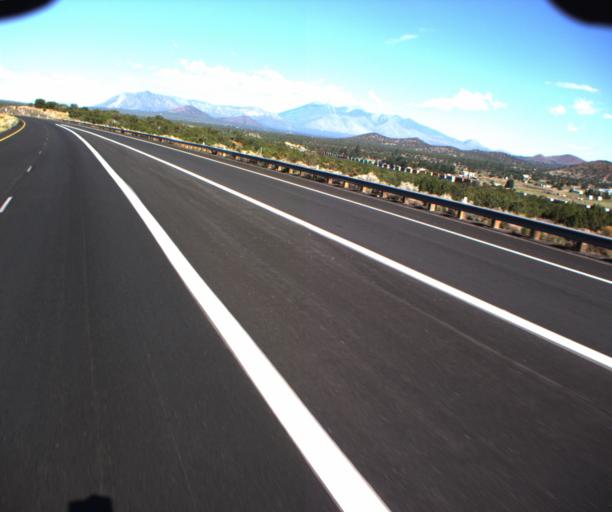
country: US
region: Arizona
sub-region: Coconino County
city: Flagstaff
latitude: 35.2029
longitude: -111.4113
